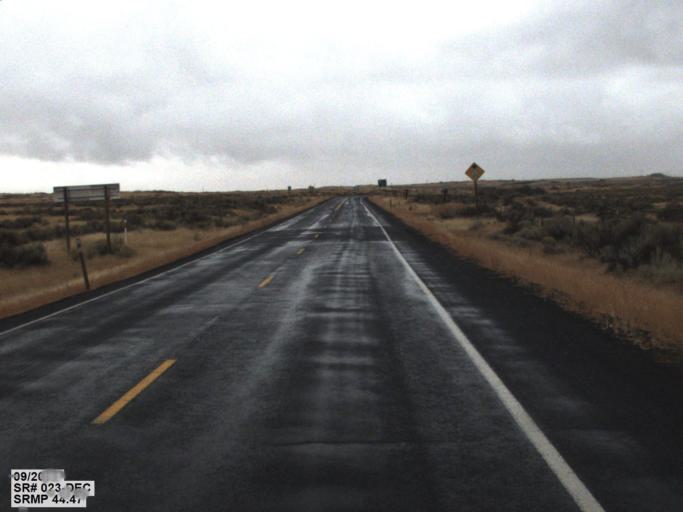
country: US
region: Washington
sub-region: Lincoln County
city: Davenport
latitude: 47.3183
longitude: -117.9764
